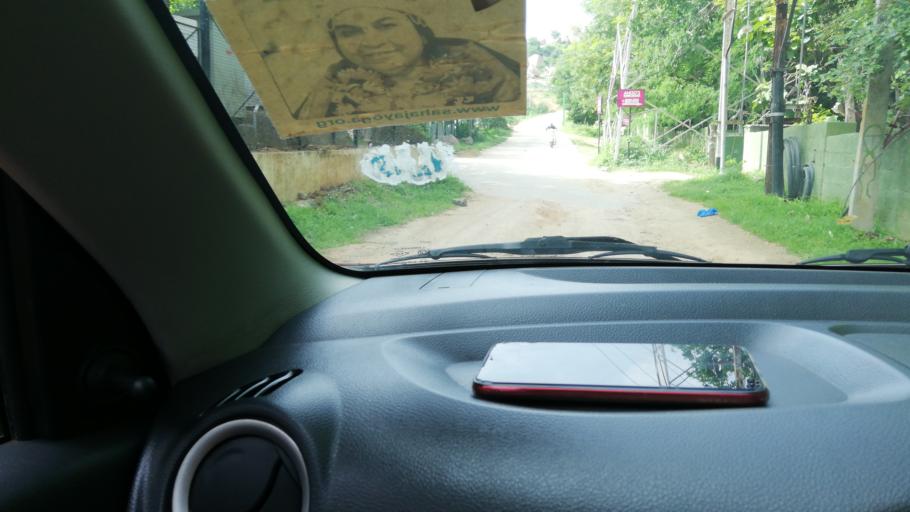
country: IN
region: Telangana
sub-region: Rangareddi
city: Kukatpalli
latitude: 17.4135
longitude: 78.3660
